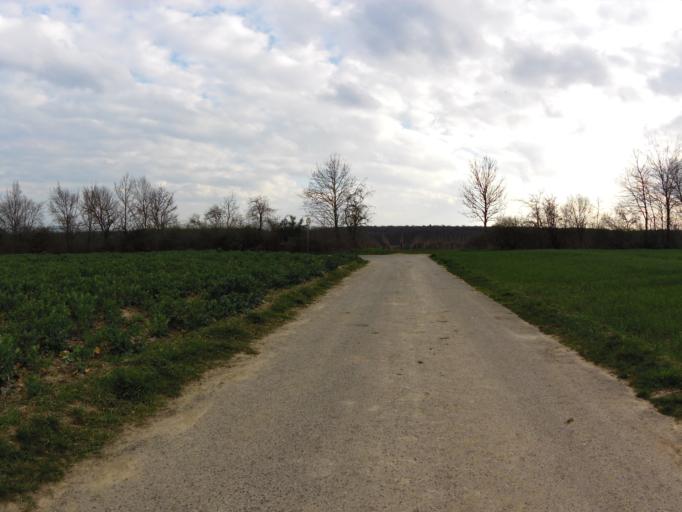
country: DE
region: Bavaria
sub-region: Regierungsbezirk Unterfranken
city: Buchbrunn
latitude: 49.7396
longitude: 10.1206
